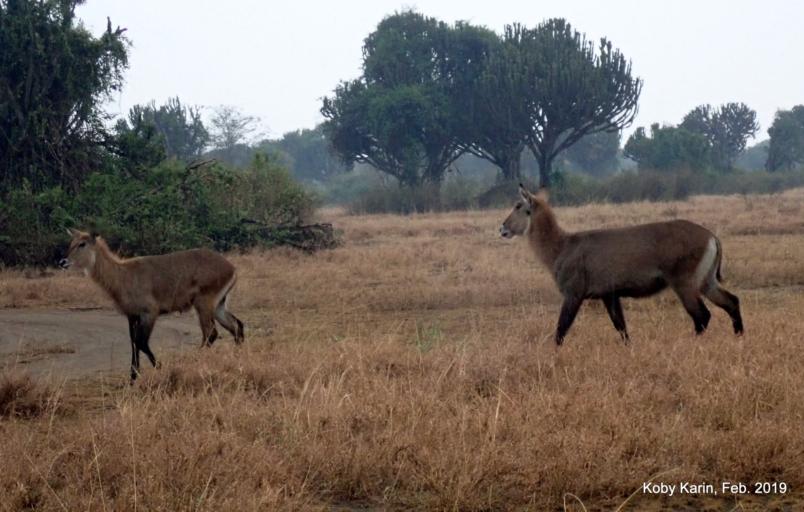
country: UG
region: Western Region
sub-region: Kasese District
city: Kasese
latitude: 0.0012
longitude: 30.0893
